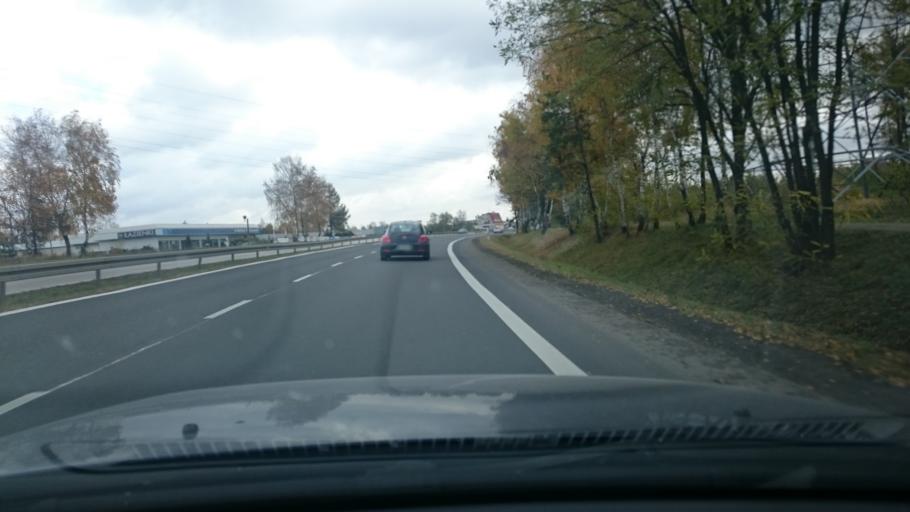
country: PL
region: Lesser Poland Voivodeship
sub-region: Powiat olkuski
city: Olkusz
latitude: 50.2875
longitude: 19.5413
